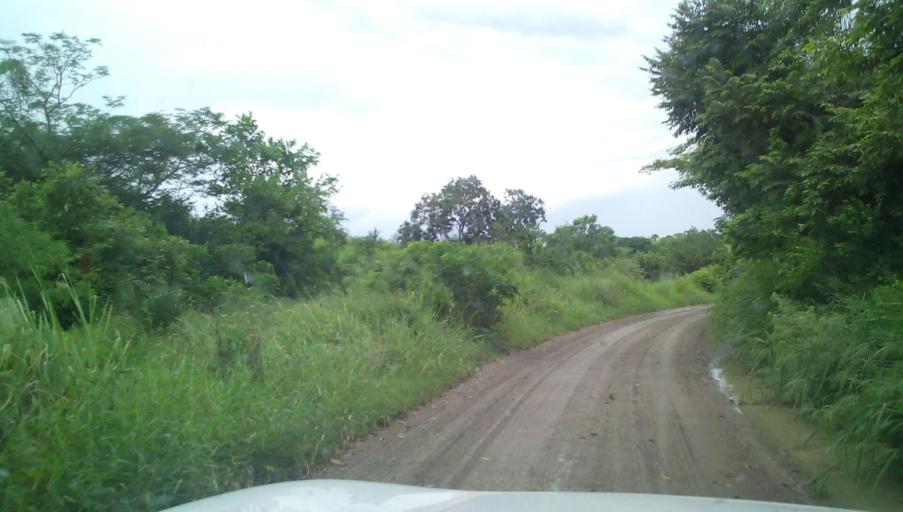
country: MX
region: Veracruz
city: Panuco
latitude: 21.8098
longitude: -98.1102
